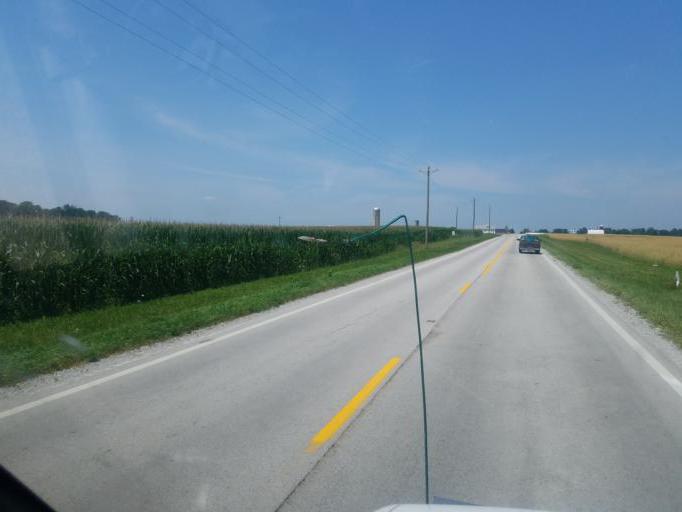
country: US
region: Ohio
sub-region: Auglaize County
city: Minster
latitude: 40.3763
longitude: -84.4340
